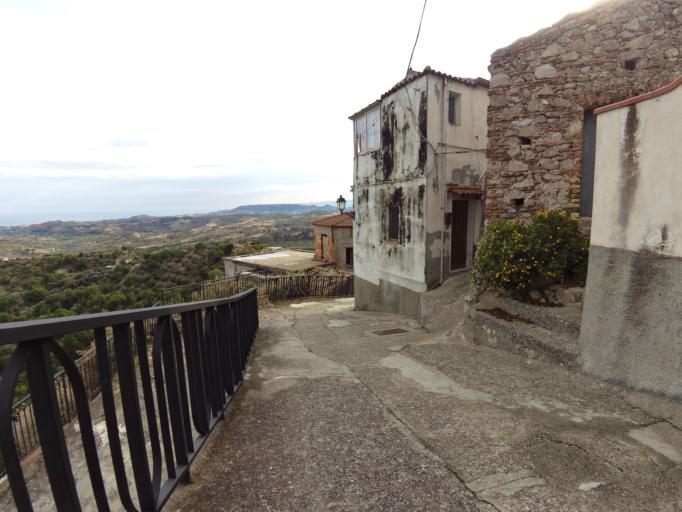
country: IT
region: Calabria
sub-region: Provincia di Reggio Calabria
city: Stignano
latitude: 38.4161
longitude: 16.4723
